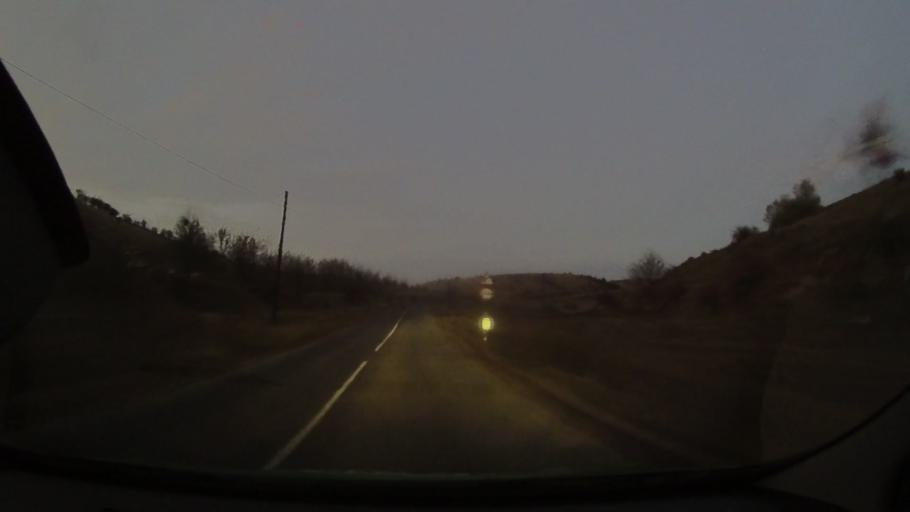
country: RO
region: Constanta
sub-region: Comuna Ion Corvin
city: Ion Corvin
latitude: 44.1183
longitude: 27.8112
